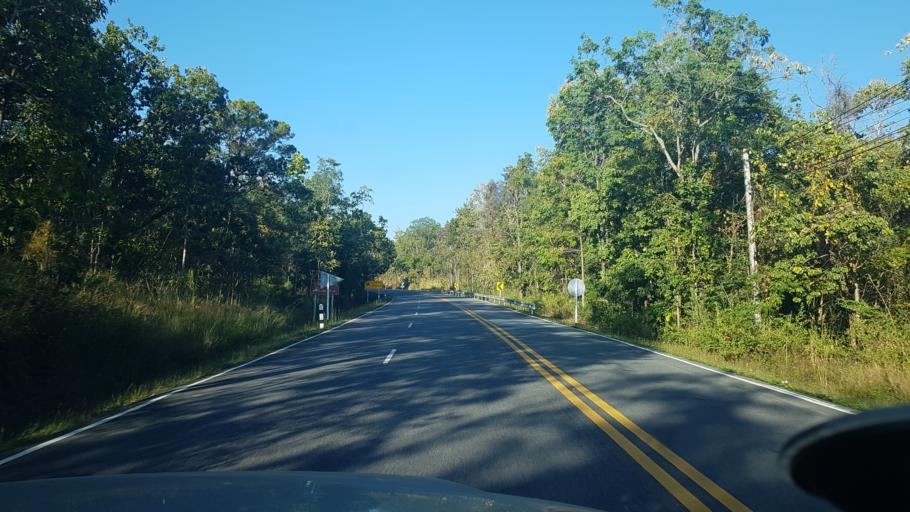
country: TH
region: Phetchabun
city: Nam Nao
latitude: 16.7023
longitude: 101.6478
